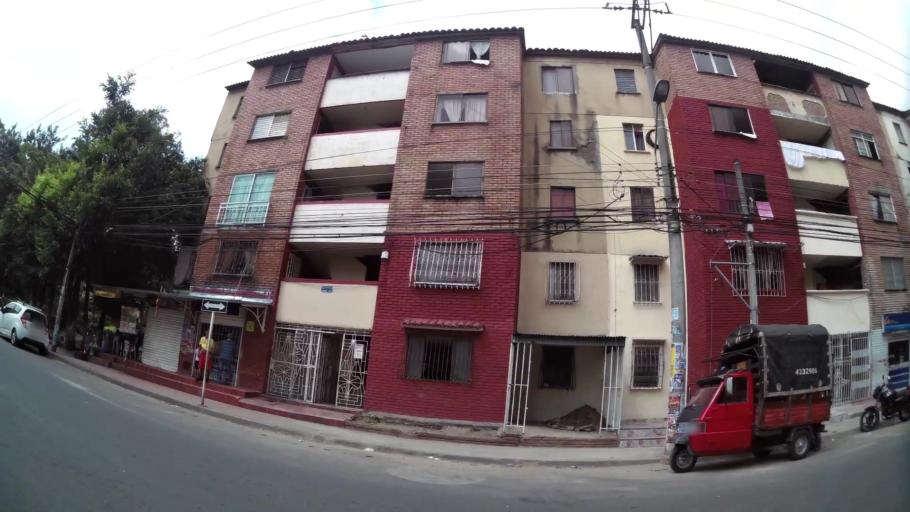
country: CO
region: Valle del Cauca
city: Cali
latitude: 3.4872
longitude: -76.4899
